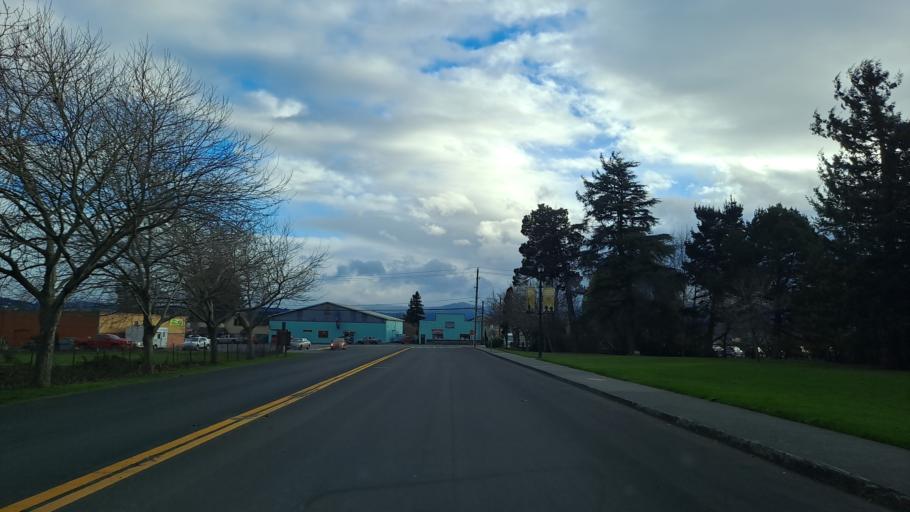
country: US
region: California
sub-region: Humboldt County
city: Fortuna
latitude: 40.5990
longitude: -124.1497
